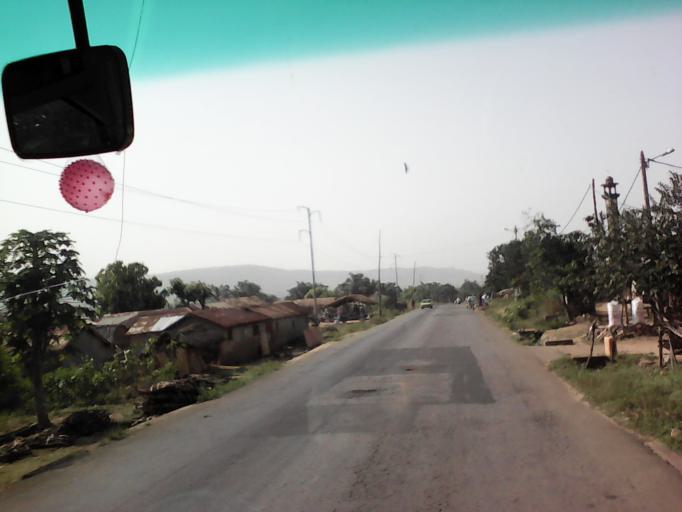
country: TG
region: Centrale
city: Sokode
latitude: 9.1104
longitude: 1.1442
